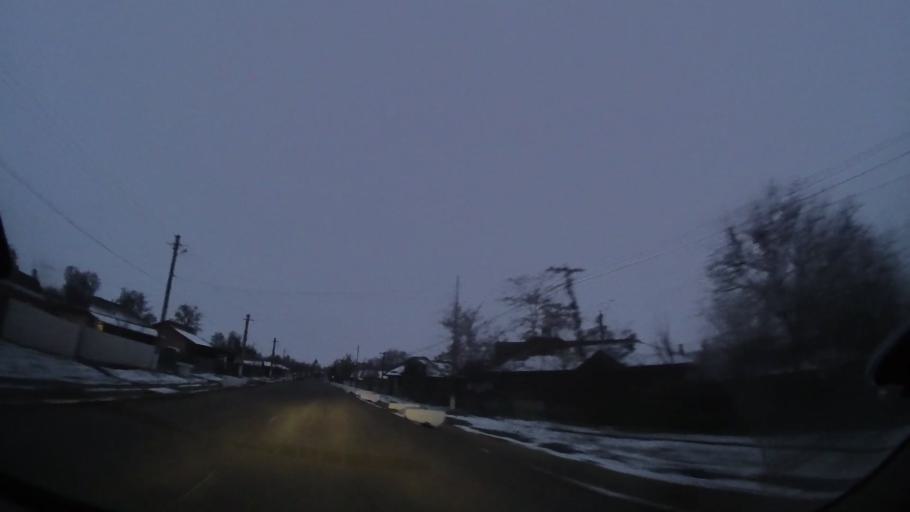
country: RO
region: Vaslui
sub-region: Comuna Dimitrie Cantemir
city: Dimitrie Cantemir
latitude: 46.5047
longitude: 28.0553
